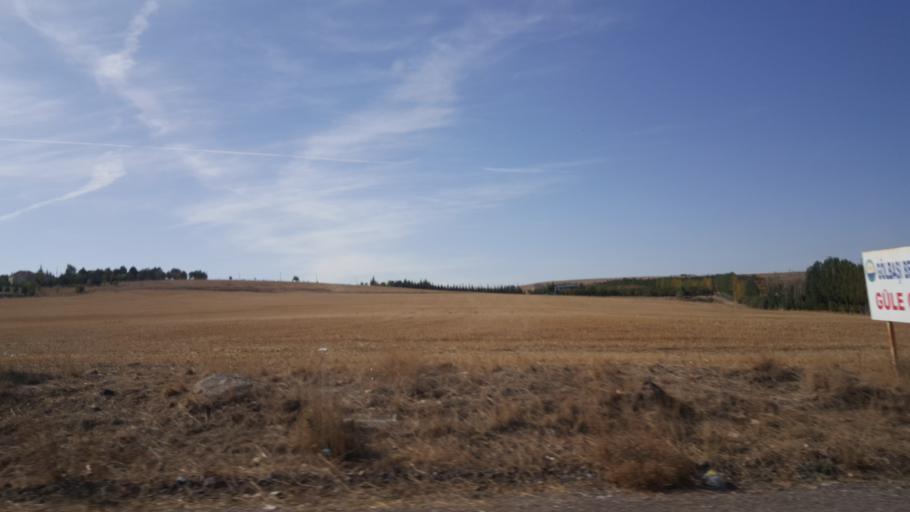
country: TR
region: Ankara
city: Ikizce
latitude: 39.6721
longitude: 32.7347
